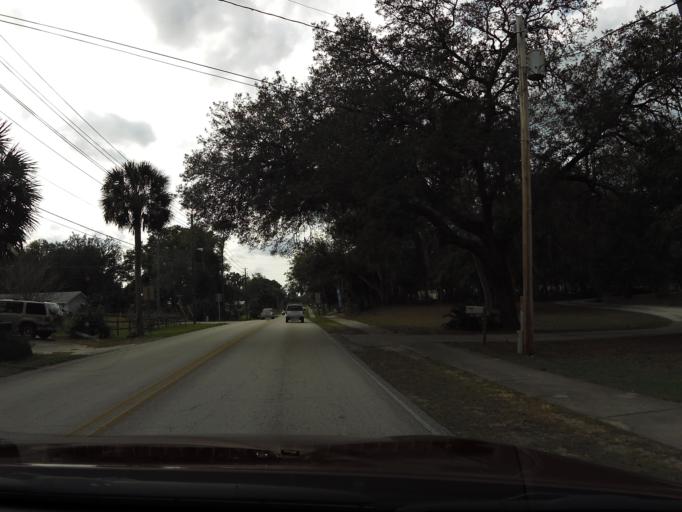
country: US
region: Florida
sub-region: Volusia County
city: Orange City
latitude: 28.9487
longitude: -81.2858
